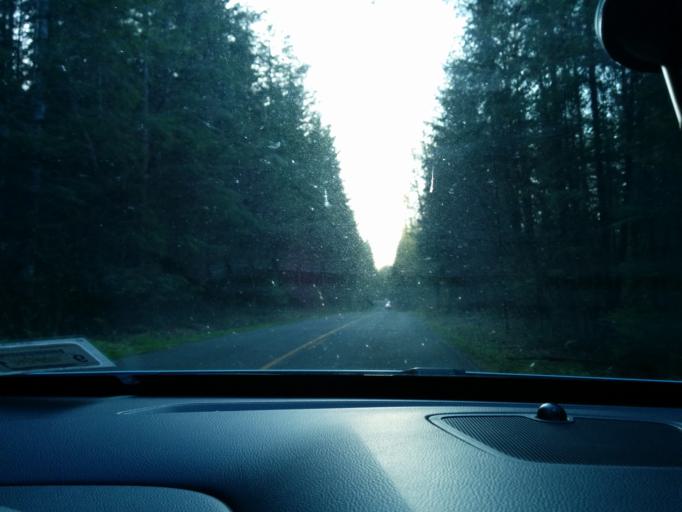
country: US
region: Washington
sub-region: Snohomish County
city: Gold Bar
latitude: 47.8957
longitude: -121.7440
